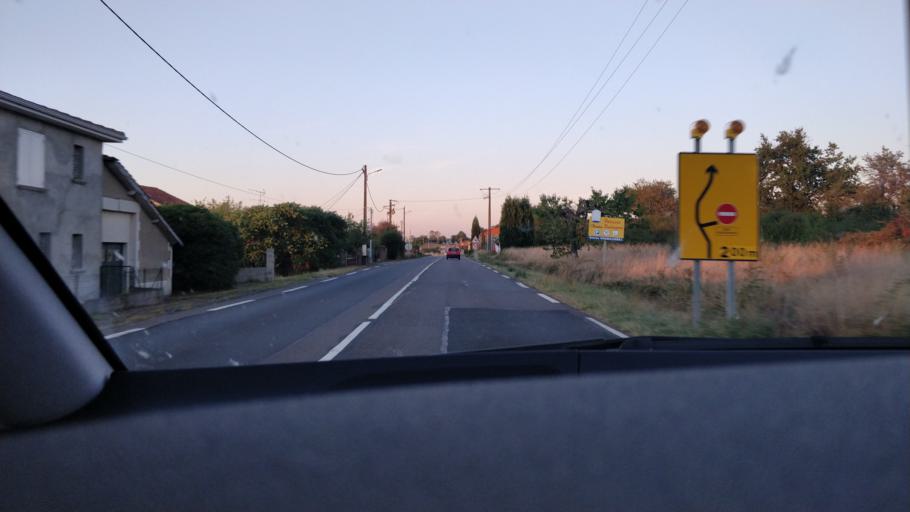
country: FR
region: Poitou-Charentes
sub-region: Departement de la Charente
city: Loubert
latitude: 45.8743
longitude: 0.5570
